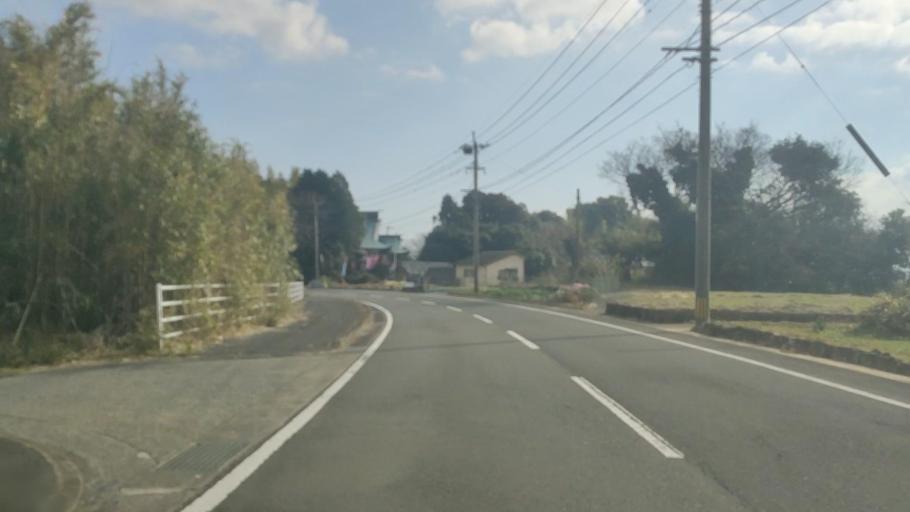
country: JP
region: Nagasaki
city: Shimabara
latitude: 32.6800
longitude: 130.2769
